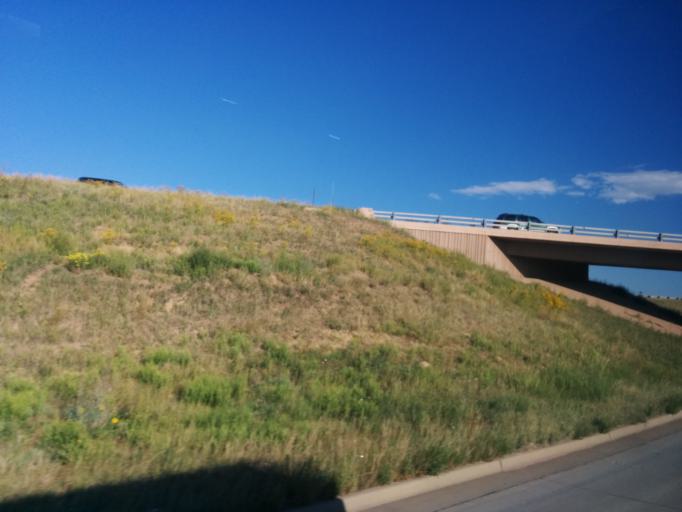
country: US
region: Colorado
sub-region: Adams County
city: Aurora
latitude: 39.7712
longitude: -104.7922
